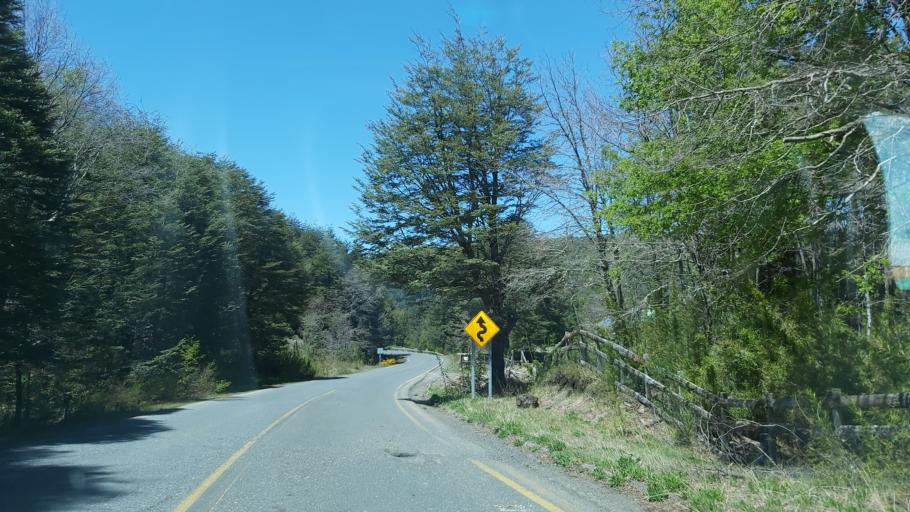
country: CL
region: Araucania
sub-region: Provincia de Cautin
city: Vilcun
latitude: -38.4680
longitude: -71.6549
